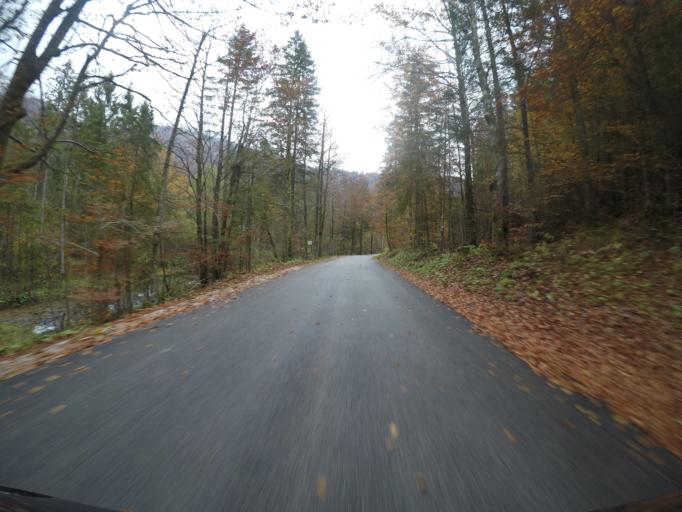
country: SI
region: Jesenice
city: Hrusica
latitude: 46.4175
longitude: 13.9880
